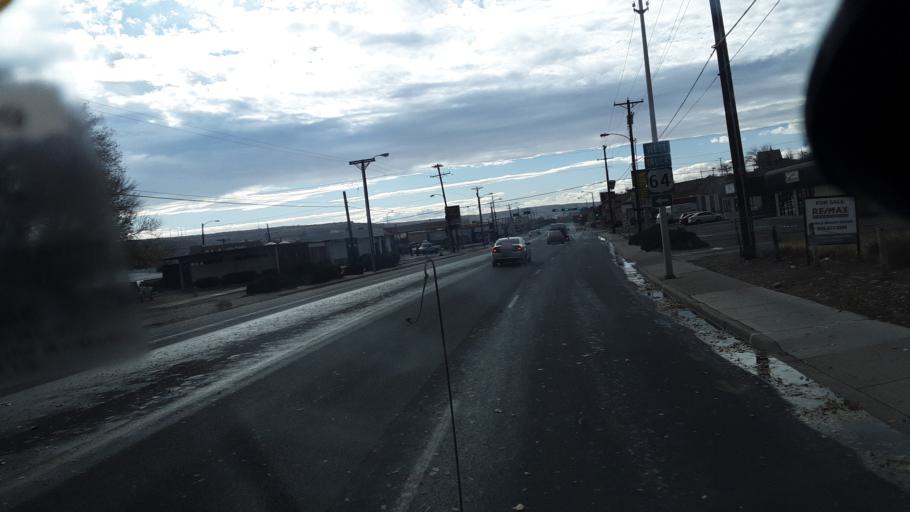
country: US
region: New Mexico
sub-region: San Juan County
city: Farmington
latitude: 36.7313
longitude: -108.1958
